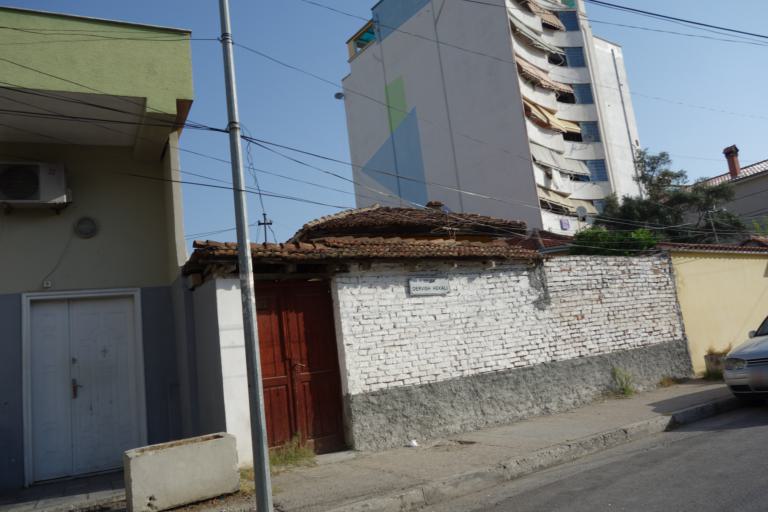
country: AL
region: Tirane
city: Tirana
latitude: 41.3331
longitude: 19.8264
